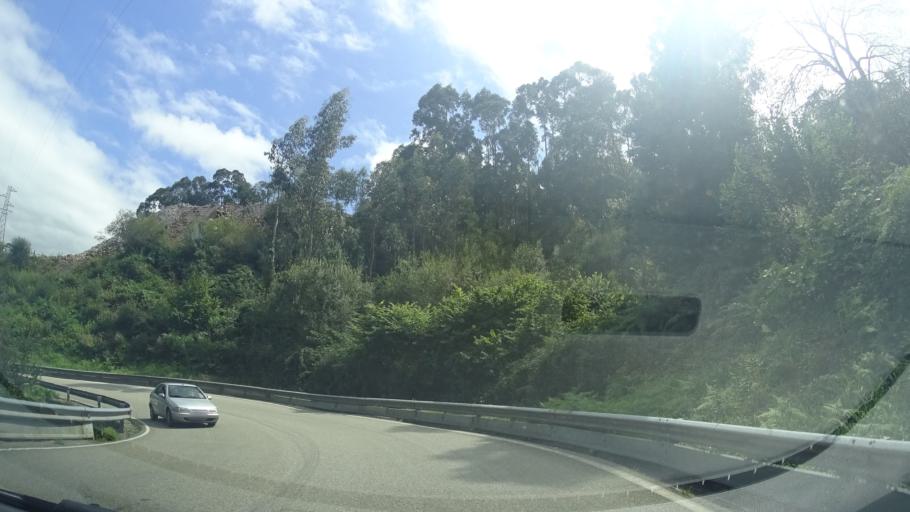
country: ES
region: Asturias
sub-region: Province of Asturias
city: Ribadesella
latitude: 43.4679
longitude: -5.1338
